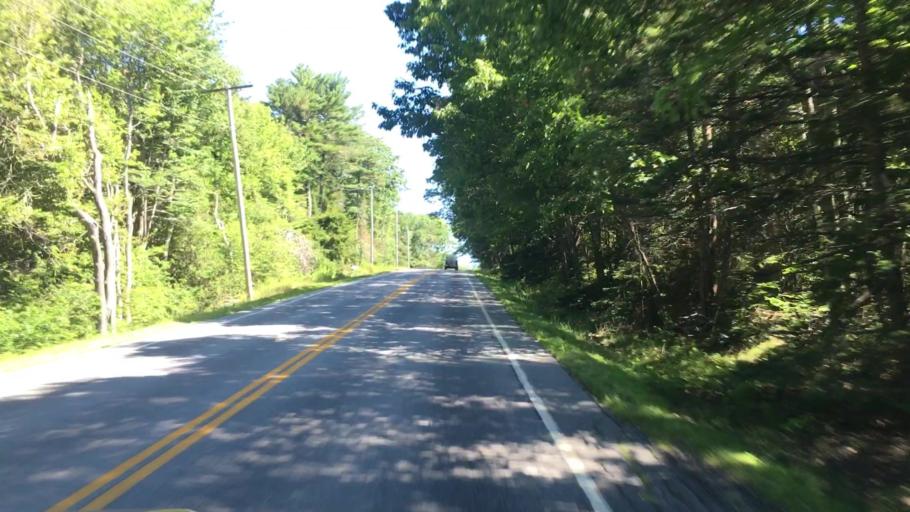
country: US
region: Maine
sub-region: Hancock County
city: Sedgwick
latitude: 44.3555
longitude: -68.6670
